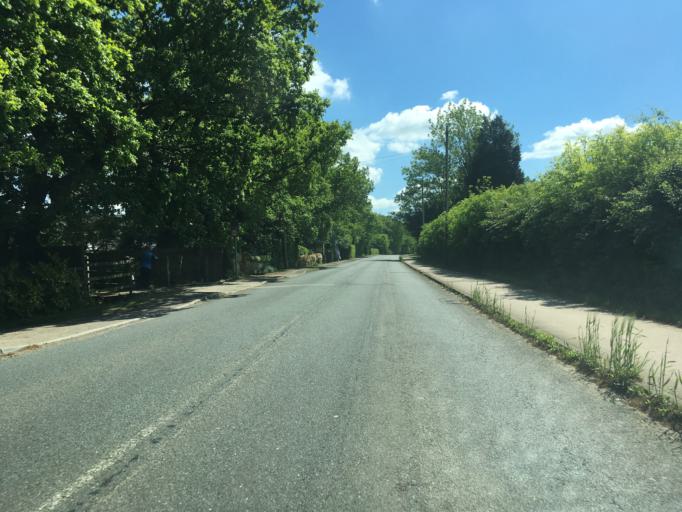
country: GB
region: England
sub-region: Milton Keynes
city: Woburn Sands
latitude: 52.0227
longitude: -0.6600
